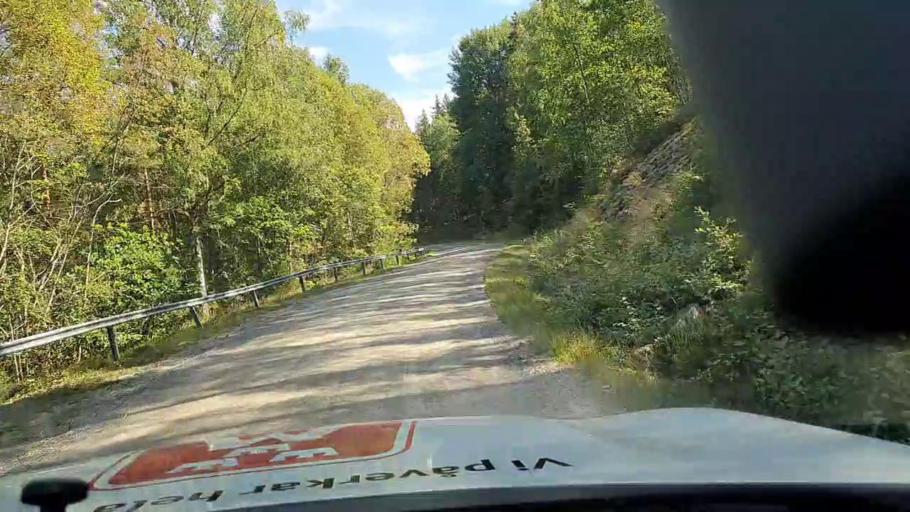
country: SE
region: Soedermanland
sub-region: Strangnas Kommun
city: Akers Styckebruk
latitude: 59.2093
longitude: 16.9115
